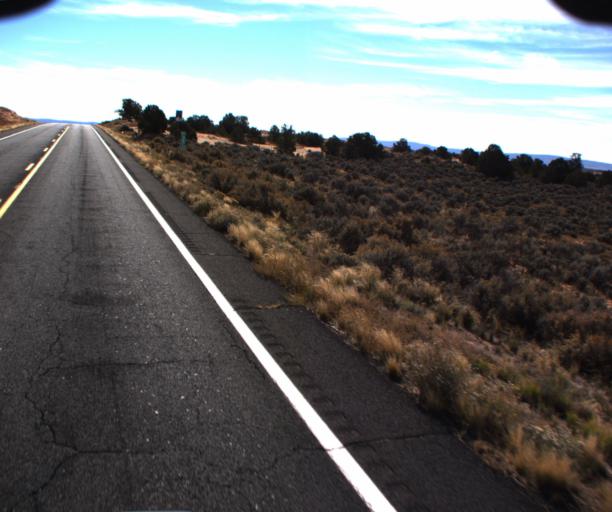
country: US
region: Arizona
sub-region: Coconino County
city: Kaibito
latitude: 36.5726
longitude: -110.7671
